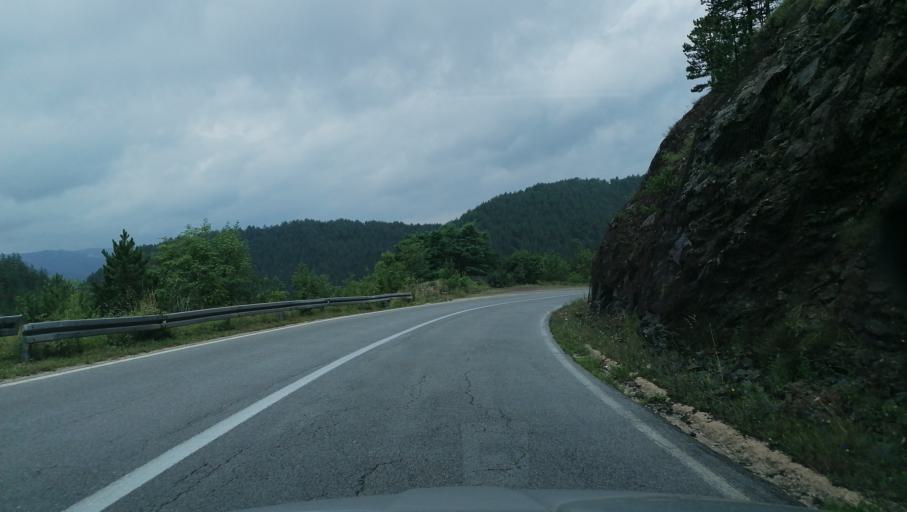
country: RS
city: Durici
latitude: 43.8217
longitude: 19.5137
